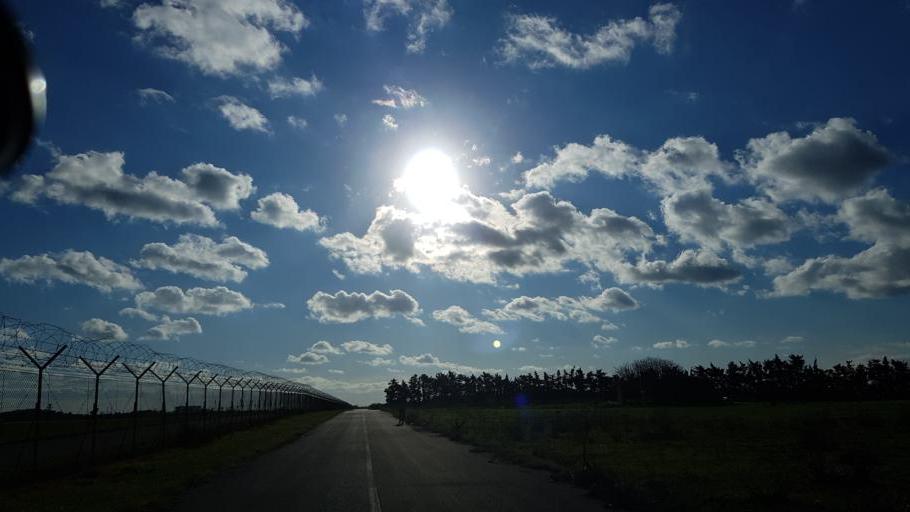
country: IT
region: Apulia
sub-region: Provincia di Brindisi
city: Materdomini
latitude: 40.6694
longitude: 17.9306
